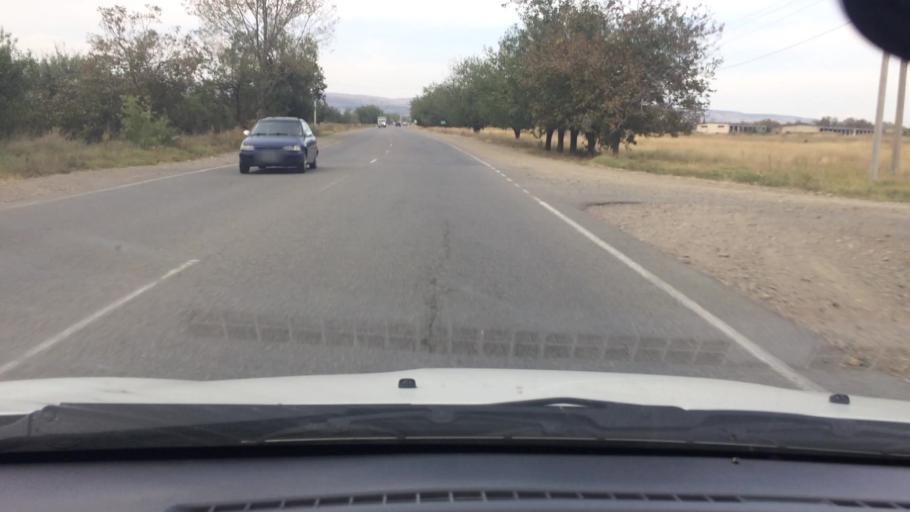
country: GE
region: Kvemo Kartli
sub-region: Marneuli
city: Marneuli
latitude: 41.5665
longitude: 44.7755
